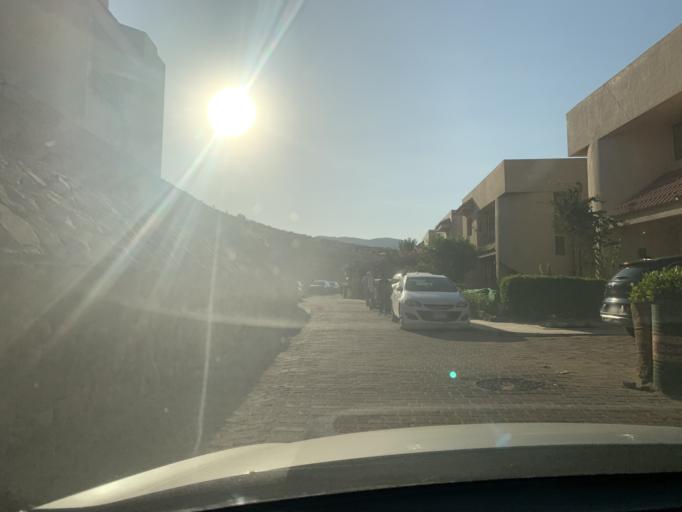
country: EG
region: As Suways
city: Ain Sukhna
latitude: 29.3740
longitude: 32.5720
